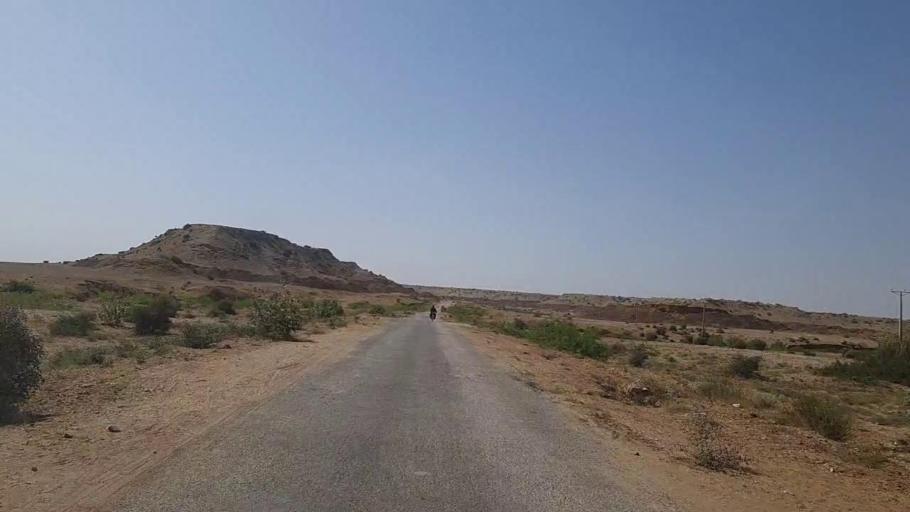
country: PK
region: Sindh
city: Kotri
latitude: 25.1597
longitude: 68.2199
